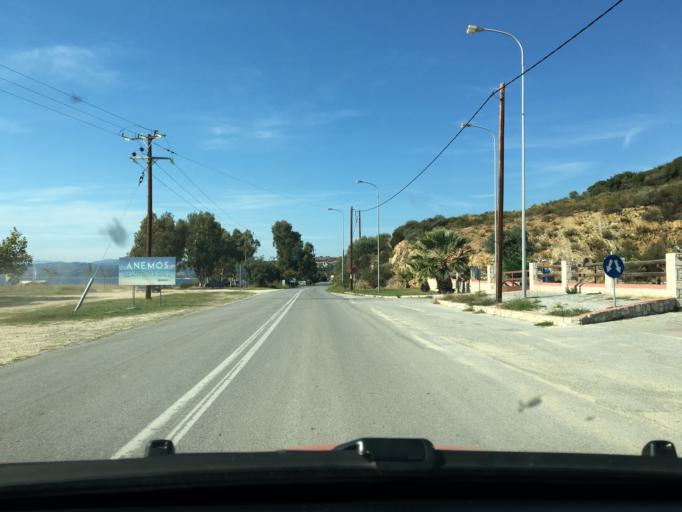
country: GR
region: Central Macedonia
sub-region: Nomos Chalkidikis
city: Ouranoupolis
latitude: 40.3434
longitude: 23.9674
